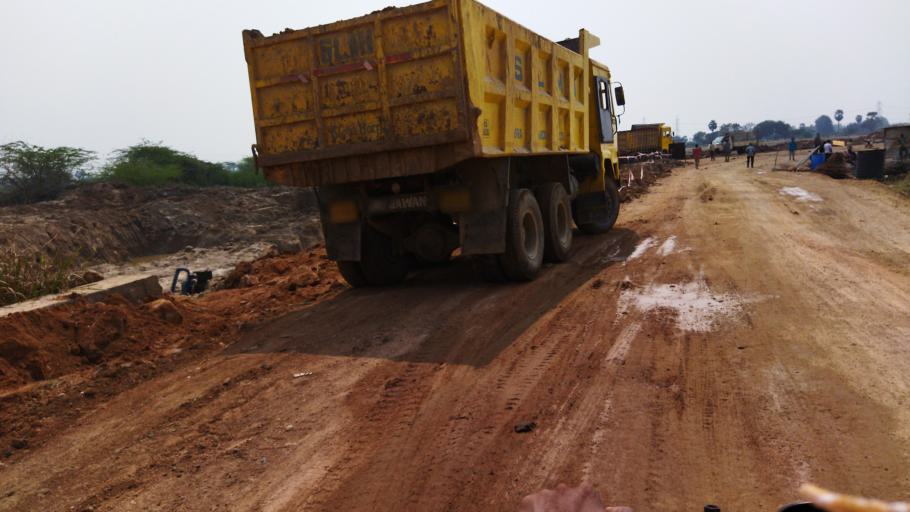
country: IN
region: Telangana
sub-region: Nalgonda
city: Nalgonda
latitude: 17.1379
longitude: 79.3856
